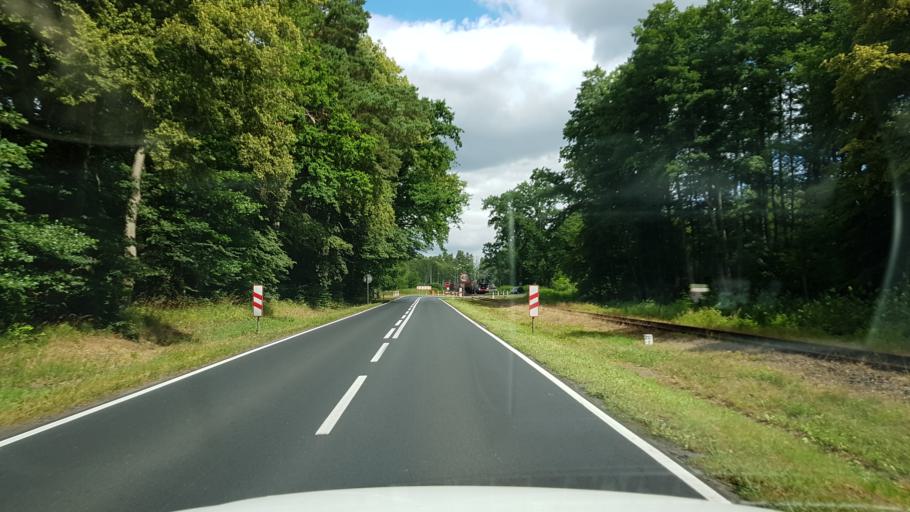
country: PL
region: West Pomeranian Voivodeship
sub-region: Powiat mysliborski
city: Debno
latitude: 52.7666
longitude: 14.7393
